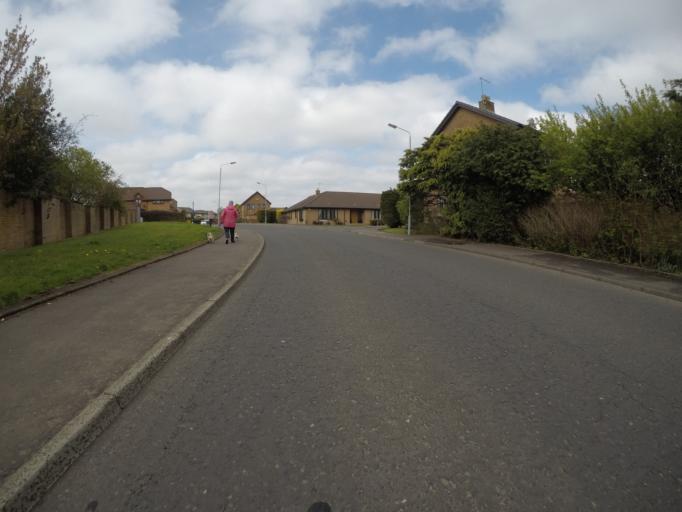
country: GB
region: Scotland
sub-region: East Renfrewshire
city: Newton Mearns
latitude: 55.7777
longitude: -4.3483
